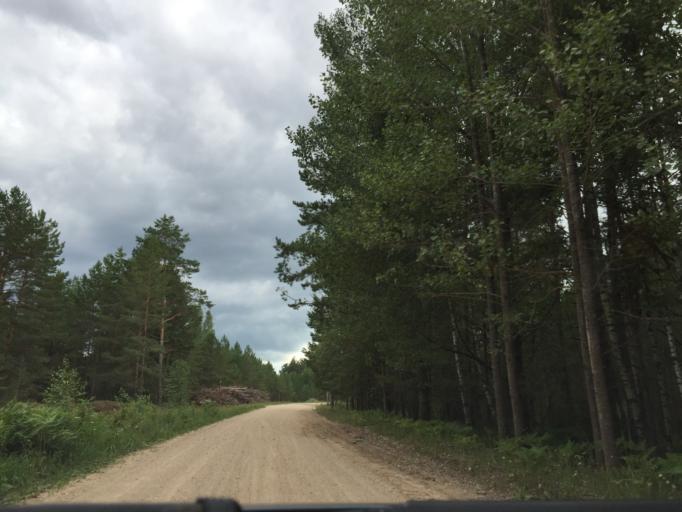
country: LV
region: Saulkrastu
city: Saulkrasti
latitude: 57.1754
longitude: 24.3815
